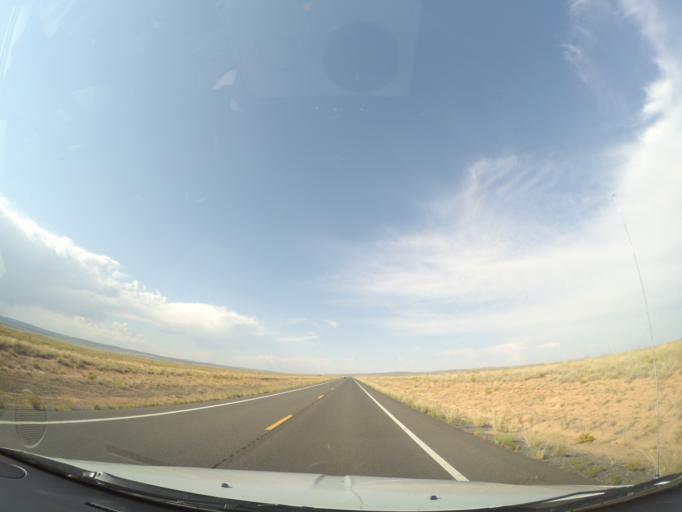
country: US
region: Arizona
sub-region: Coconino County
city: Tuba City
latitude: 36.3836
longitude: -111.4193
